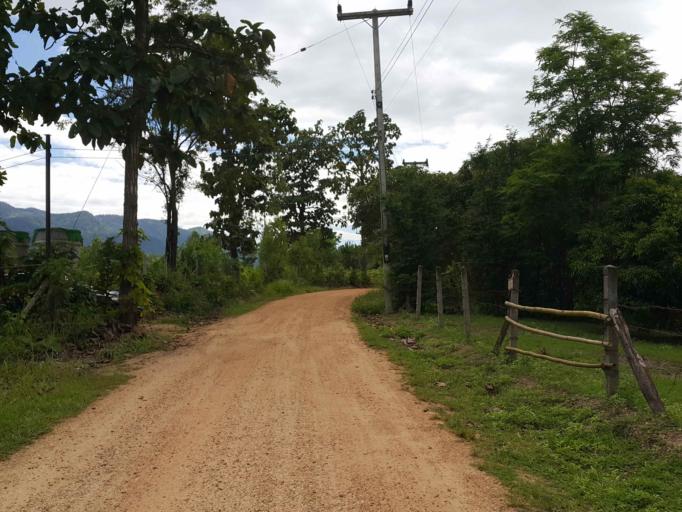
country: TH
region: Chiang Mai
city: San Sai
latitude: 18.9471
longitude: 98.9107
